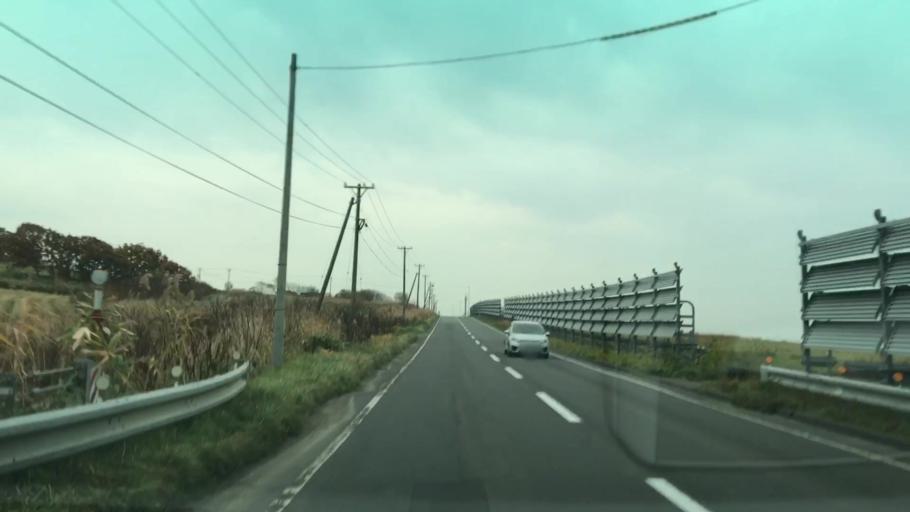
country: JP
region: Hokkaido
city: Ishikari
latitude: 43.3471
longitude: 141.4244
